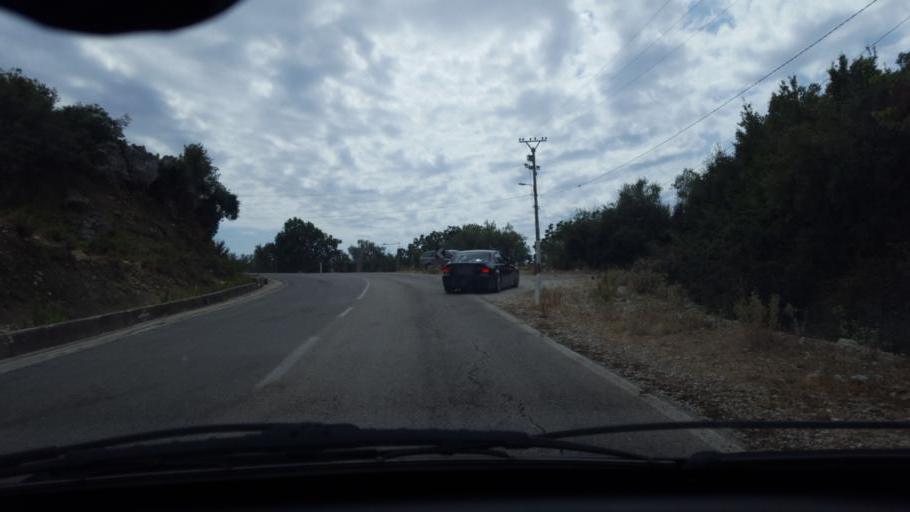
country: AL
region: Vlore
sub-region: Rrethi i Sarandes
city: Lukove
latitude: 40.0486
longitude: 19.8704
